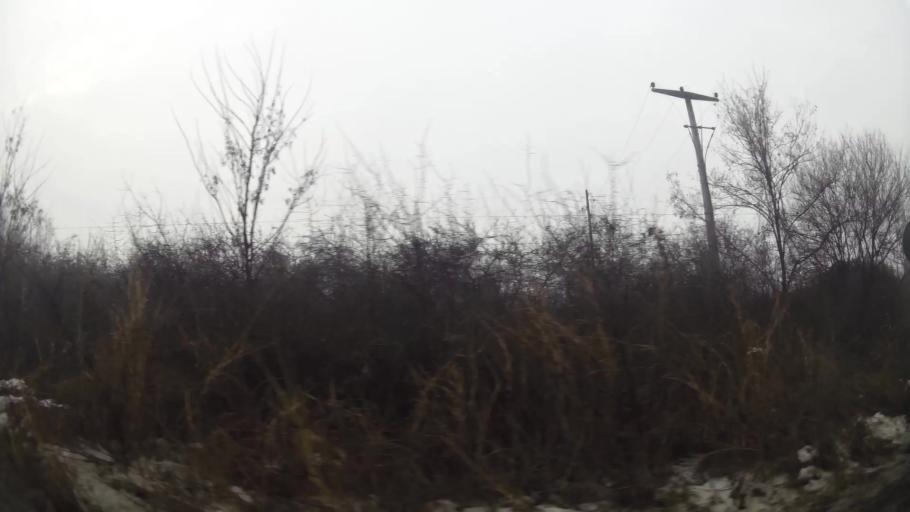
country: MK
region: Ilinden
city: Idrizovo
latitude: 41.9507
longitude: 21.5856
